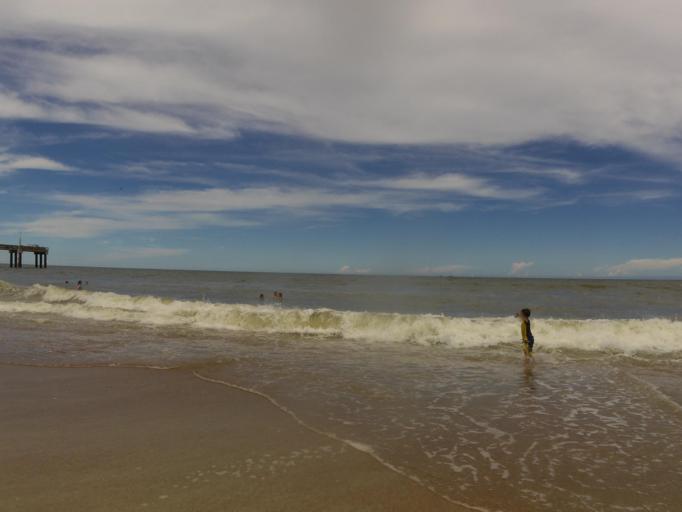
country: US
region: Florida
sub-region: Saint Johns County
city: Saint Augustine Beach
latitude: 29.8556
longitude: -81.2650
